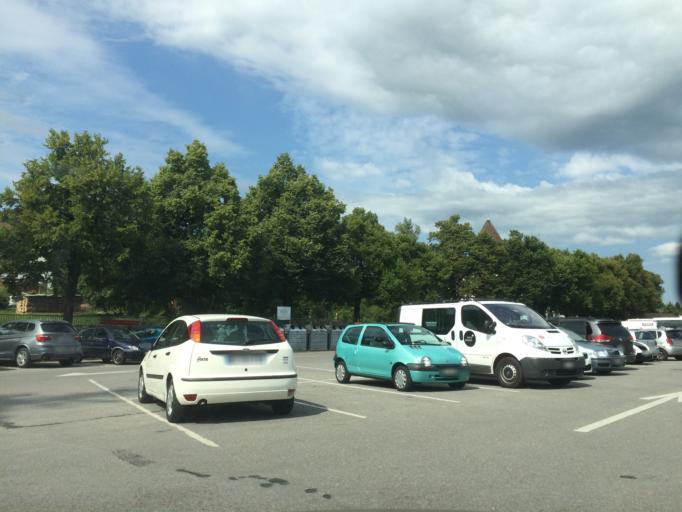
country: CH
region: Appenzell Innerrhoden
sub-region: Appenzell Inner Rhodes
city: Appenzell
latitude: 47.3302
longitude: 9.4134
